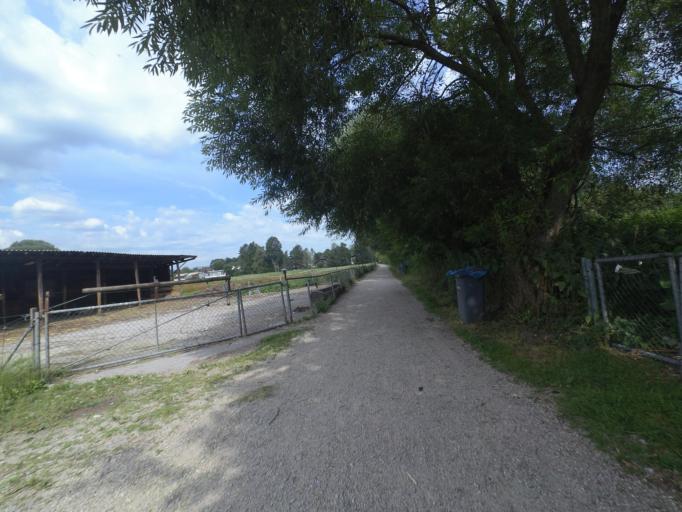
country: AT
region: Salzburg
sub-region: Salzburg Stadt
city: Salzburg
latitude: 47.7915
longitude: 13.0392
